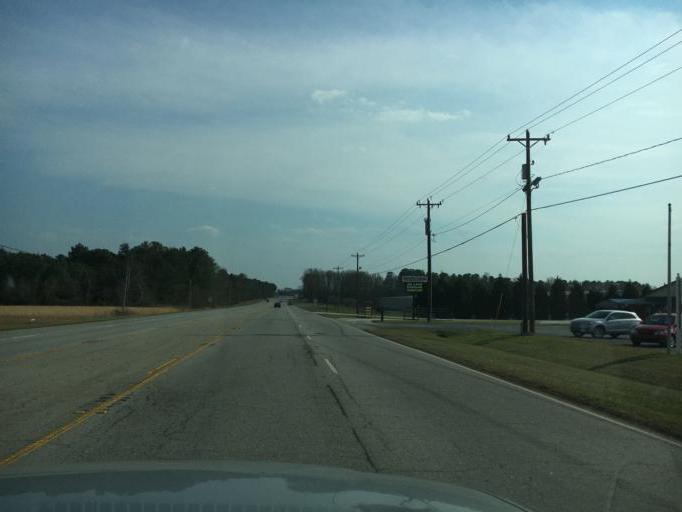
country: US
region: South Carolina
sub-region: Spartanburg County
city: Mayo
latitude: 35.1045
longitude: -81.8562
